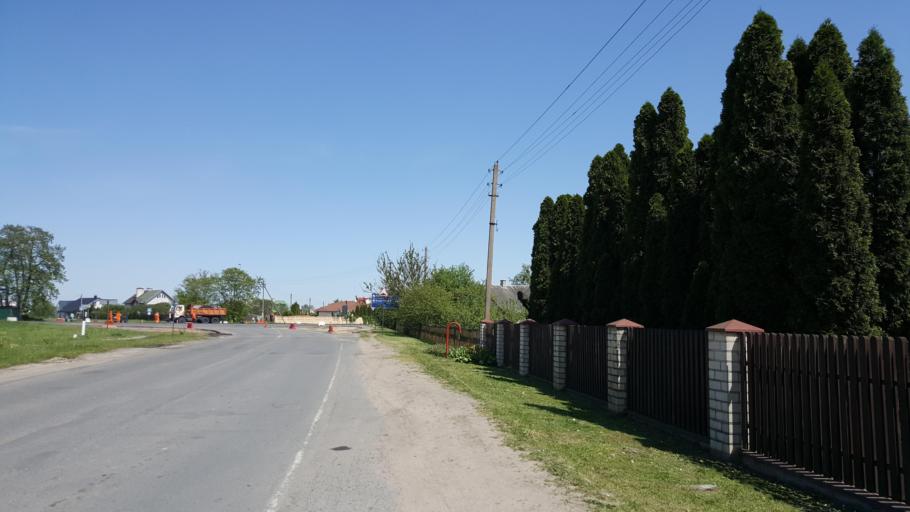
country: BY
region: Brest
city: Brest
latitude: 52.1606
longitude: 23.6639
